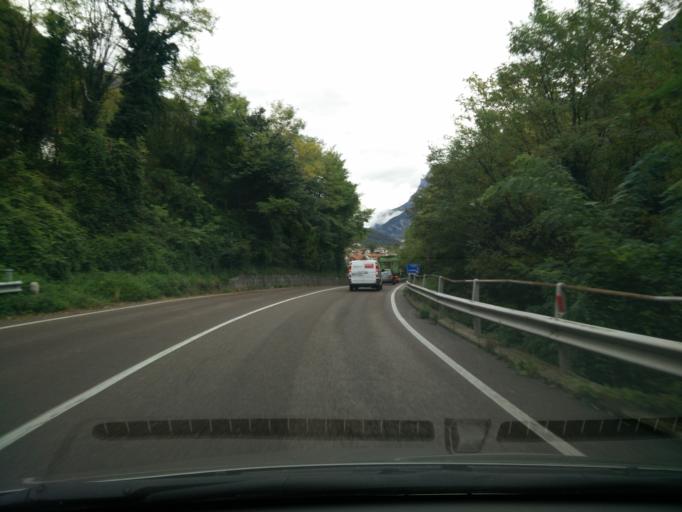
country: IT
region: Veneto
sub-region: Provincia di Belluno
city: Castello Lavazzo
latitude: 46.2802
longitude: 12.3029
